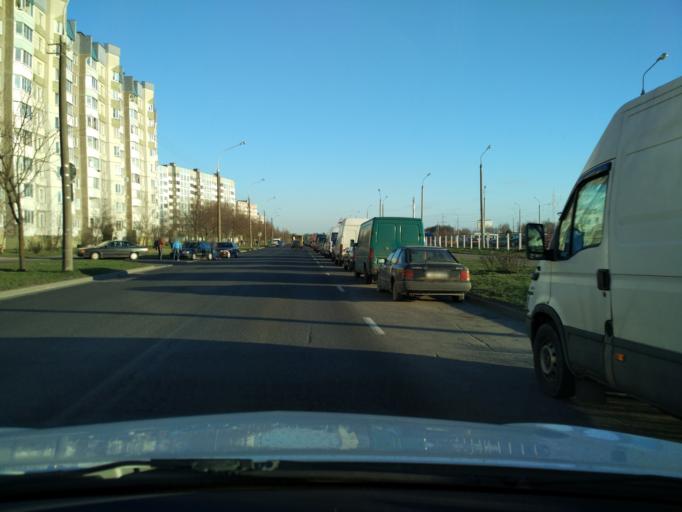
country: BY
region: Minsk
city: Malinovka
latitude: 53.8633
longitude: 27.4279
